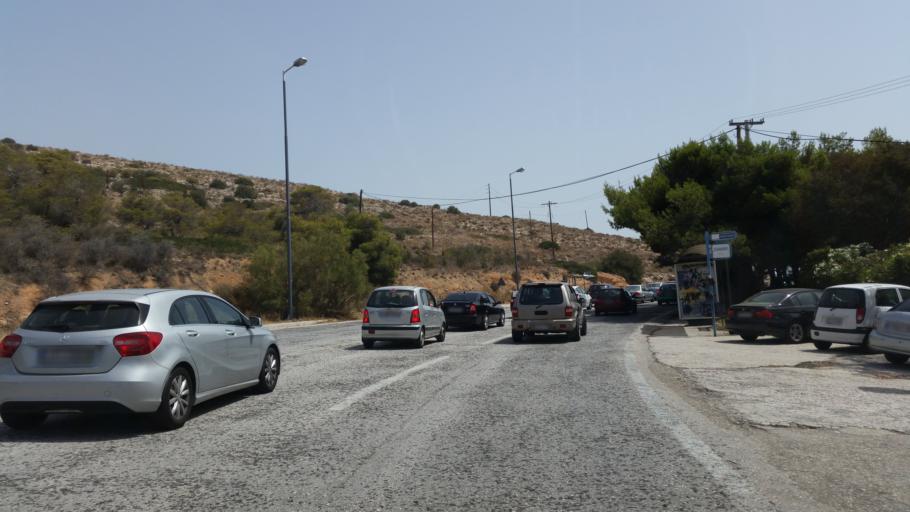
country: GR
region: Attica
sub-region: Nomarchia Anatolikis Attikis
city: Vouliagmeni
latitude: 37.8072
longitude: 23.7988
